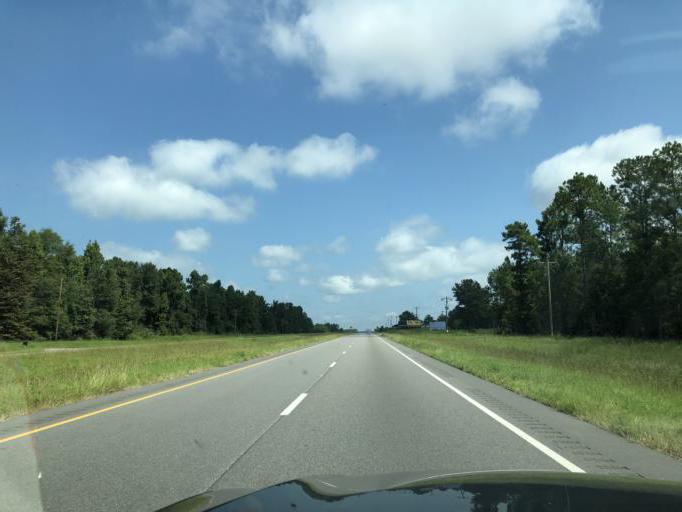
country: US
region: Alabama
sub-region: Houston County
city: Rehobeth
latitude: 31.0422
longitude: -85.4061
